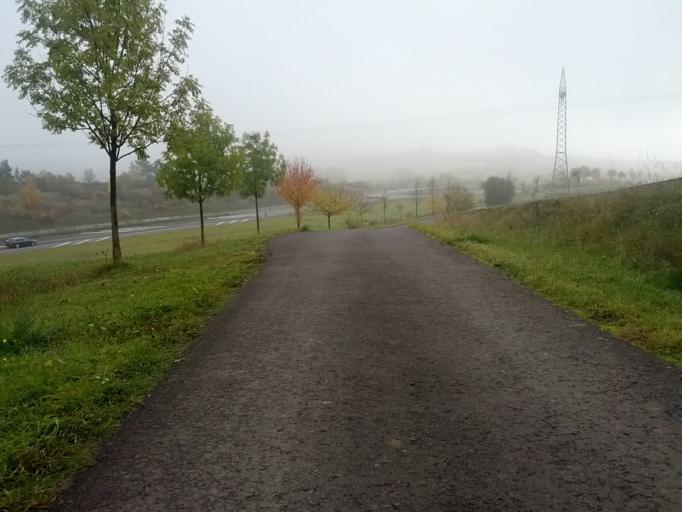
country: DE
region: Thuringia
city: Thal
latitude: 50.9704
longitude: 10.3754
